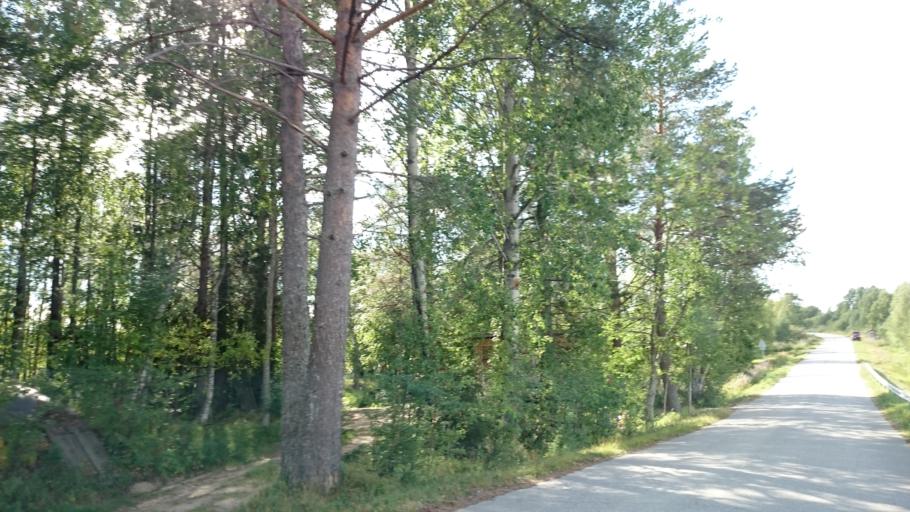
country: FI
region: Kainuu
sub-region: Kehys-Kainuu
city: Suomussalmi
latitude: 64.7363
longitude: 29.4486
